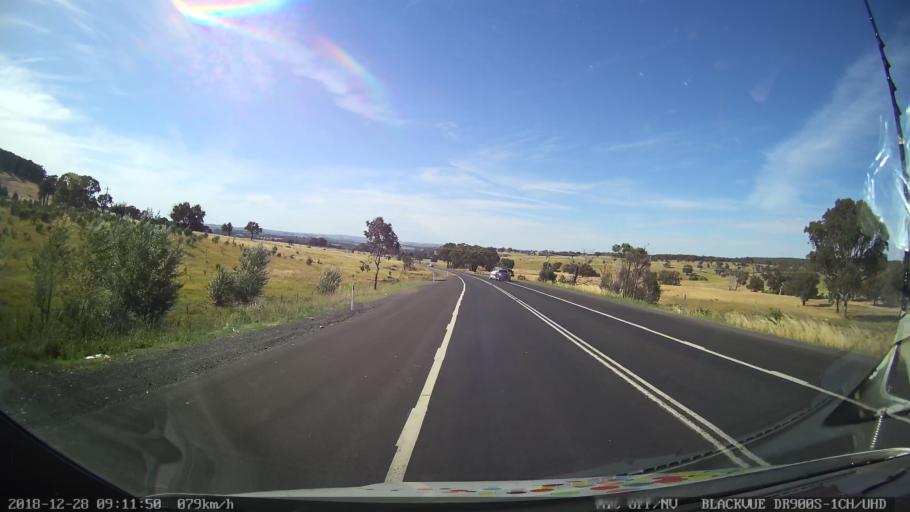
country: AU
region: New South Wales
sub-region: Upper Lachlan Shire
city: Crookwell
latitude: -34.2482
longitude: 149.3386
